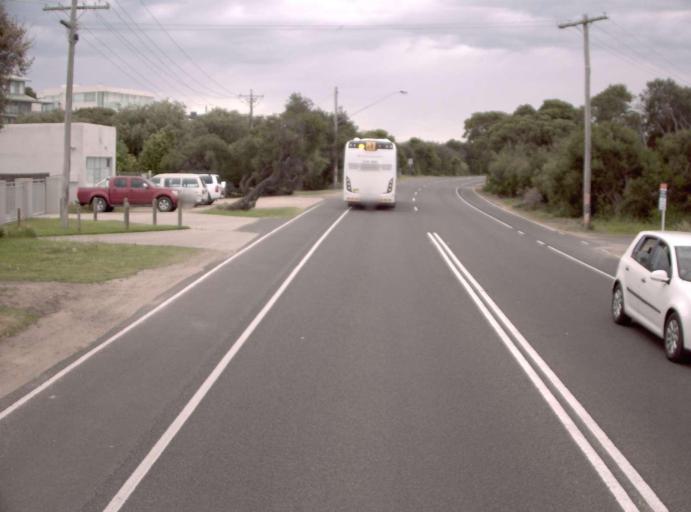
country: AU
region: Victoria
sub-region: Mornington Peninsula
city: Blairgowrie
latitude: -38.3569
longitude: 144.7665
